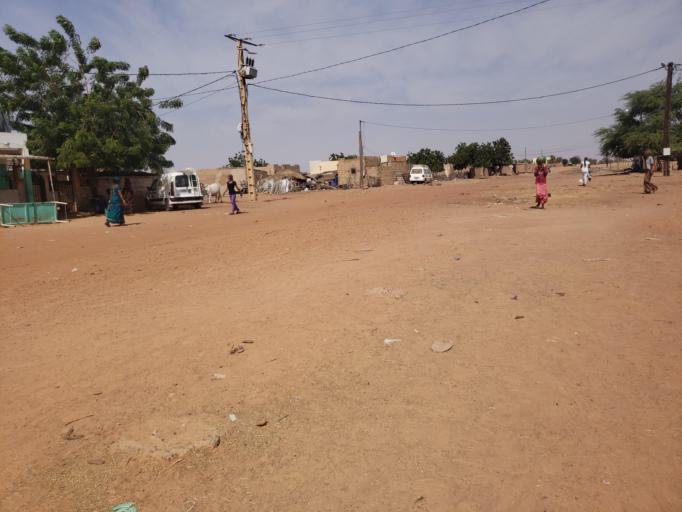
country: SN
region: Matam
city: Ranerou
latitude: 15.2991
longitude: -13.9626
